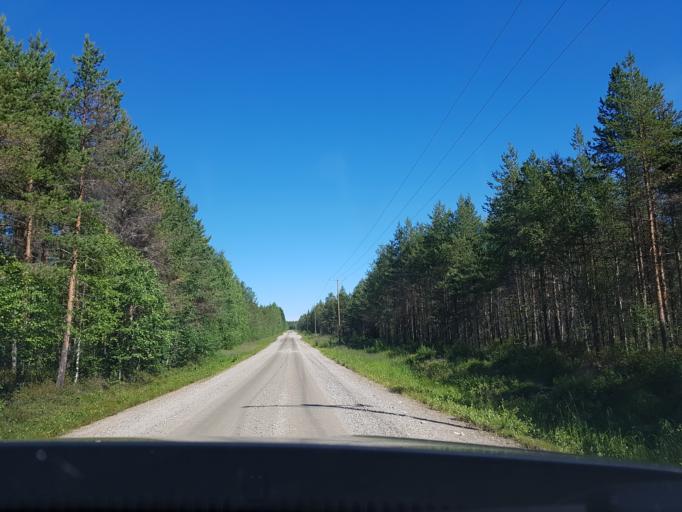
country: FI
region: Kainuu
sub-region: Kehys-Kainuu
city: Kuhmo
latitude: 64.1841
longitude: 29.5952
